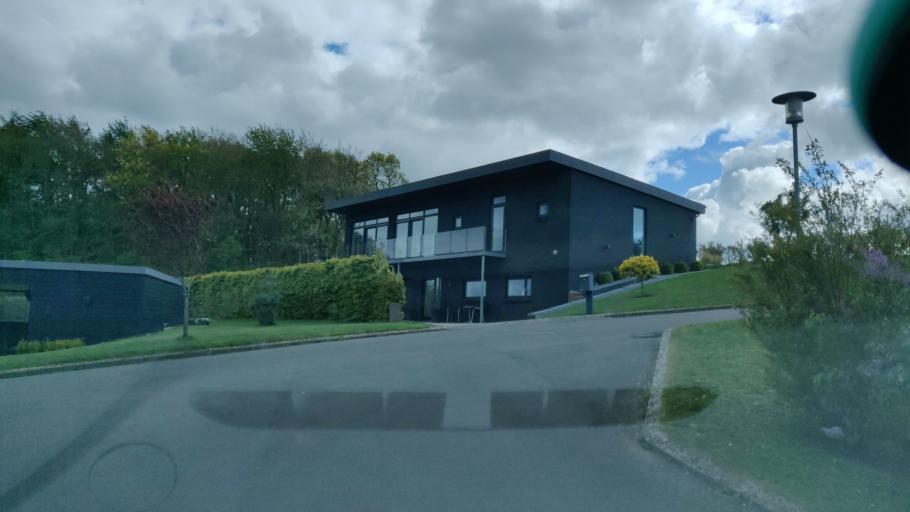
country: DK
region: South Denmark
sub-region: Kolding Kommune
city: Kolding
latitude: 55.5643
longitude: 9.4154
